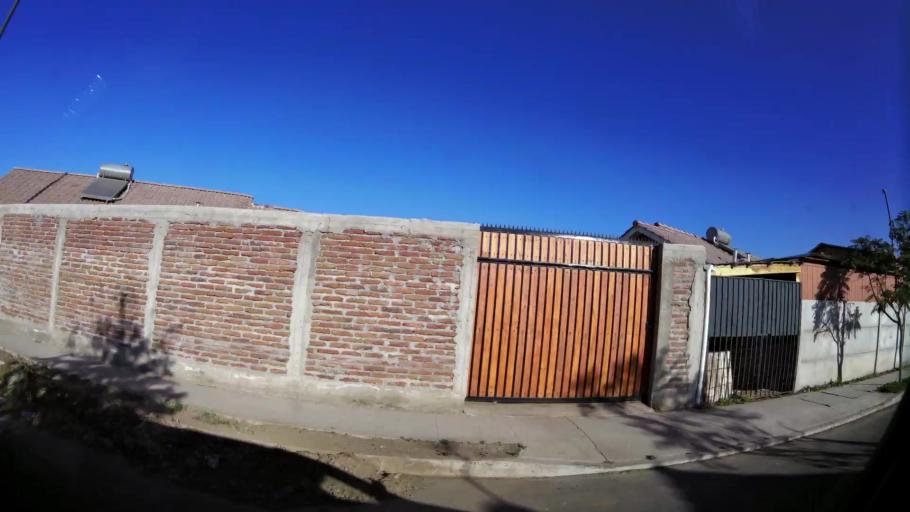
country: CL
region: Santiago Metropolitan
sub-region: Provincia de Talagante
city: Penaflor
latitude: -33.6004
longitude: -70.8566
